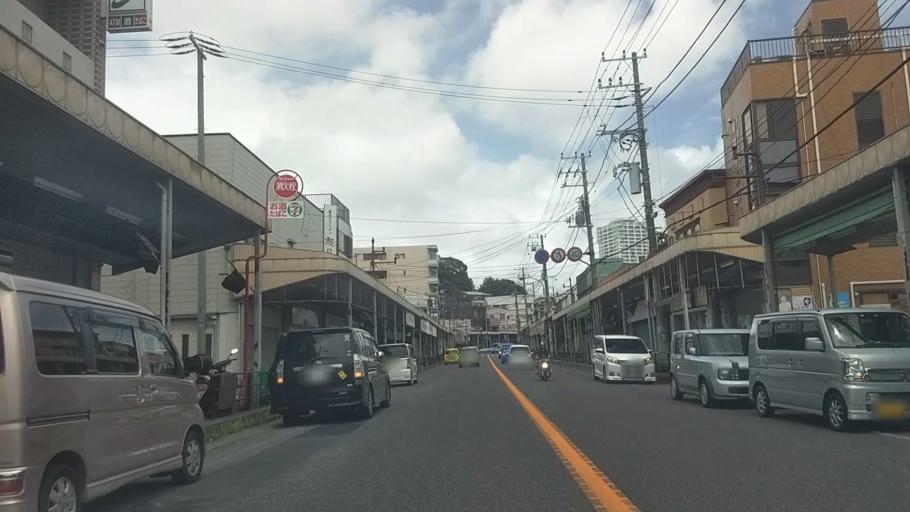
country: JP
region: Kanagawa
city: Yokosuka
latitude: 35.2745
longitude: 139.6700
